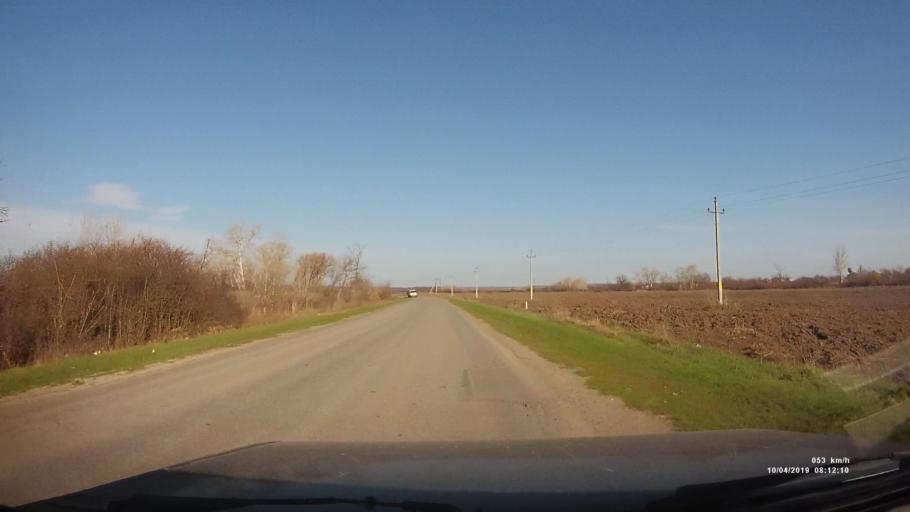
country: RU
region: Rostov
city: Masalovka
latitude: 48.3610
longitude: 40.2600
